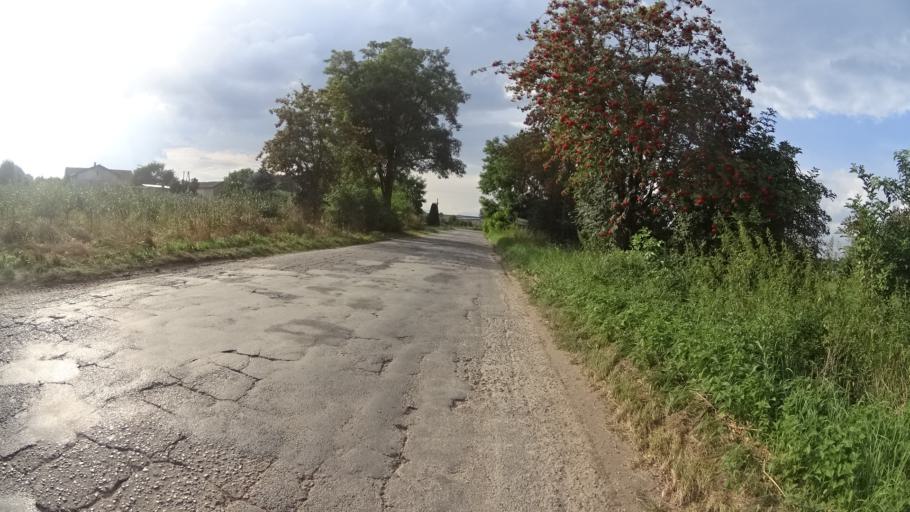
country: PL
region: Masovian Voivodeship
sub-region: Powiat grojecki
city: Mogielnica
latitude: 51.6674
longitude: 20.7397
